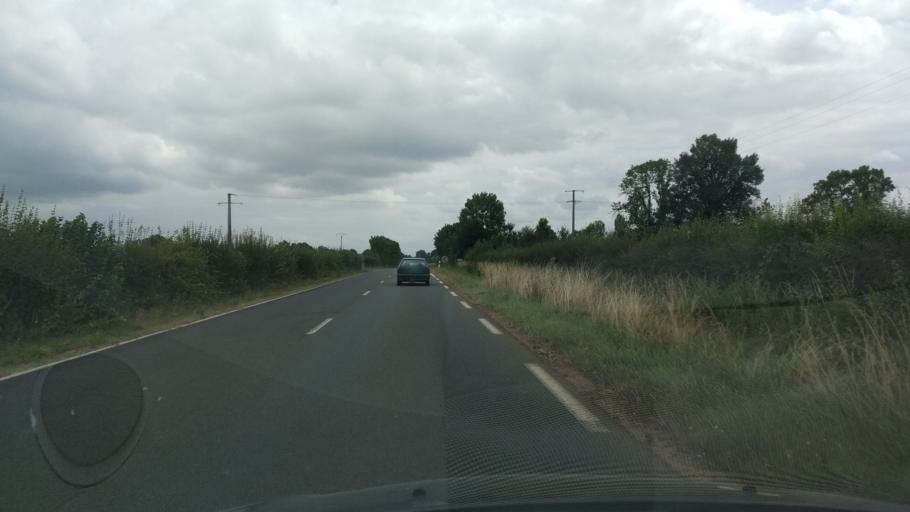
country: FR
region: Poitou-Charentes
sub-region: Departement de la Vienne
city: La Villedieu-du-Clain
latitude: 46.4179
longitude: 0.3840
